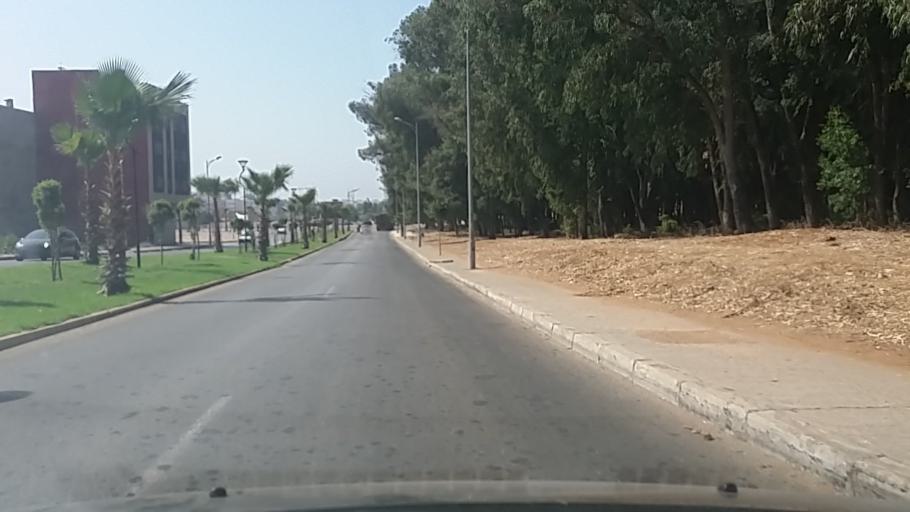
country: MA
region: Gharb-Chrarda-Beni Hssen
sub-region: Kenitra Province
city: Kenitra
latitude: 34.2501
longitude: -6.6151
